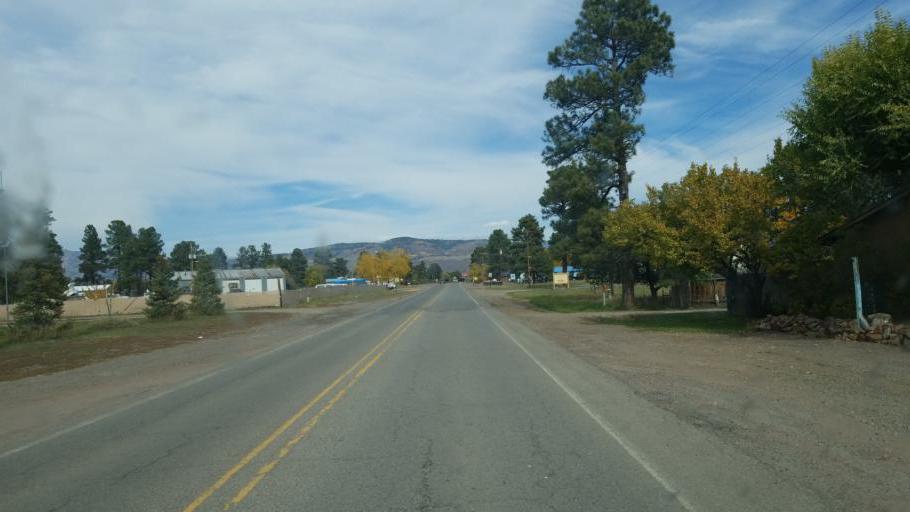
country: US
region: New Mexico
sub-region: Rio Arriba County
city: Chama
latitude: 36.8926
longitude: -106.5824
